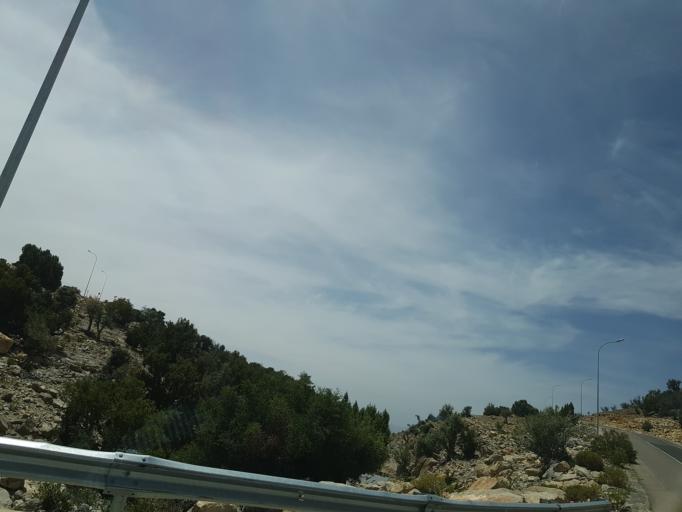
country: OM
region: Al Batinah
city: Bayt al `Awabi
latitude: 23.1350
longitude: 57.5983
